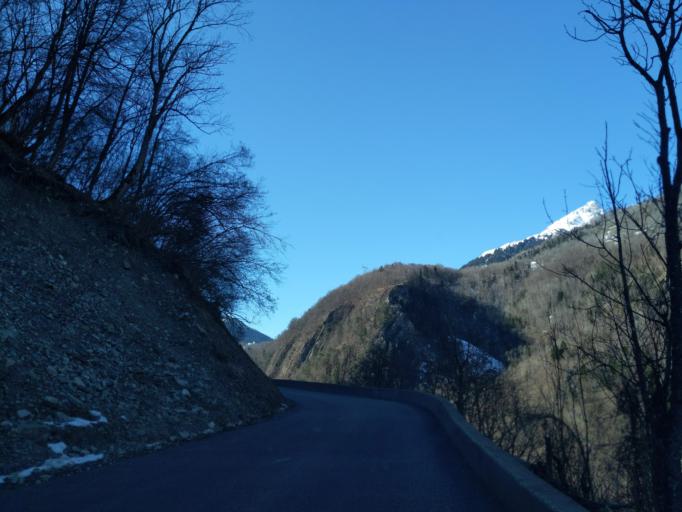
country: FR
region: Rhone-Alpes
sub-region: Departement de la Savoie
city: Salins-les-Thermes
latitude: 45.4444
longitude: 6.5033
